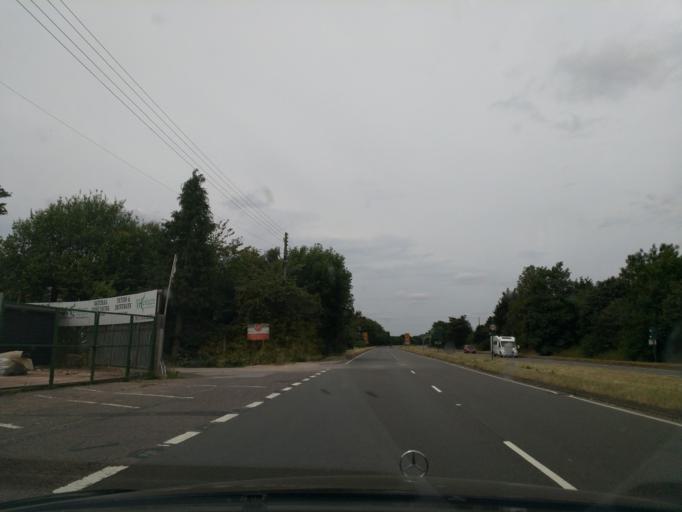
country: GB
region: England
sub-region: Solihull
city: Barston
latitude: 52.4164
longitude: -1.6762
